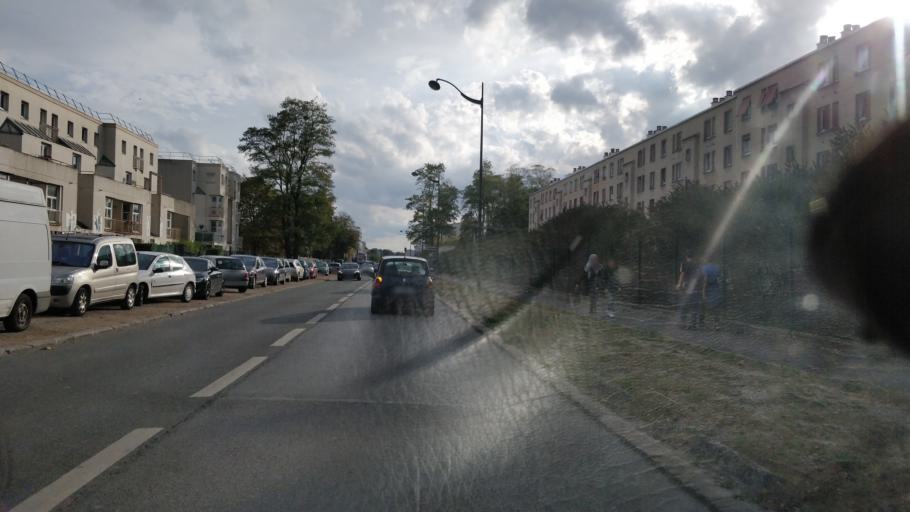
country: FR
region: Ile-de-France
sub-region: Departement de Seine-Saint-Denis
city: Clichy-sous-Bois
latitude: 48.9078
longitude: 2.5500
